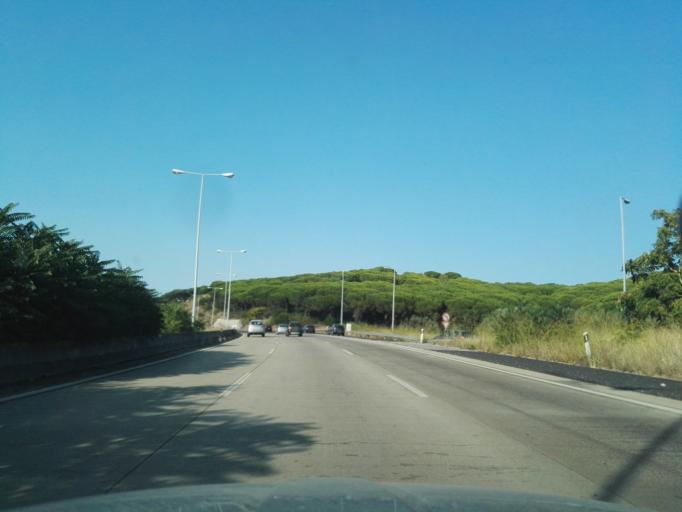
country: PT
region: Lisbon
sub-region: Oeiras
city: Alges
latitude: 38.7061
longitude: -9.2233
